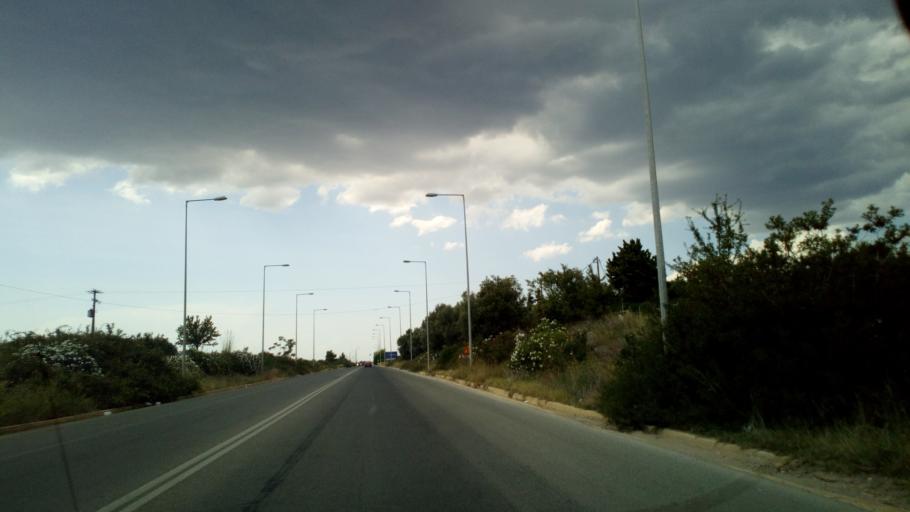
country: GR
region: Central Macedonia
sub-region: Nomos Chalkidikis
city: Kalyves Polygyrou
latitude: 40.2782
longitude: 23.4367
